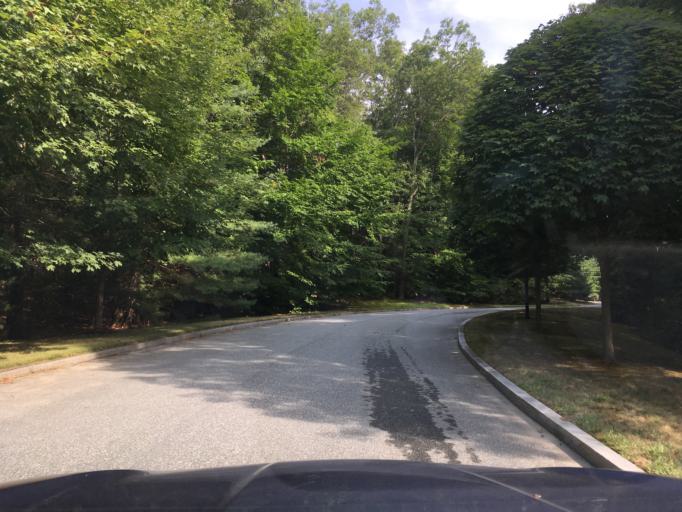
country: US
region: Rhode Island
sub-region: Kent County
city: West Warwick
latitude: 41.6421
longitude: -71.5182
